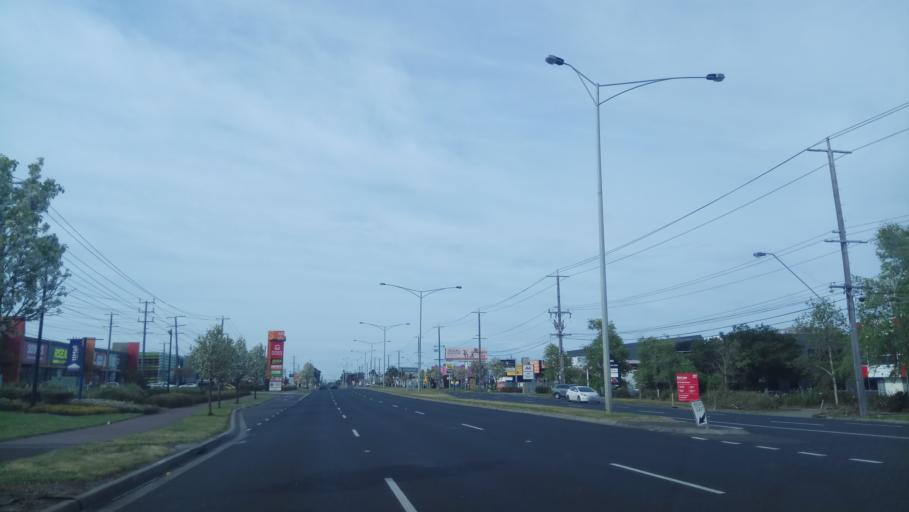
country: AU
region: Victoria
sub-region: Monash
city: Oakleigh South
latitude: -37.9474
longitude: 145.0773
